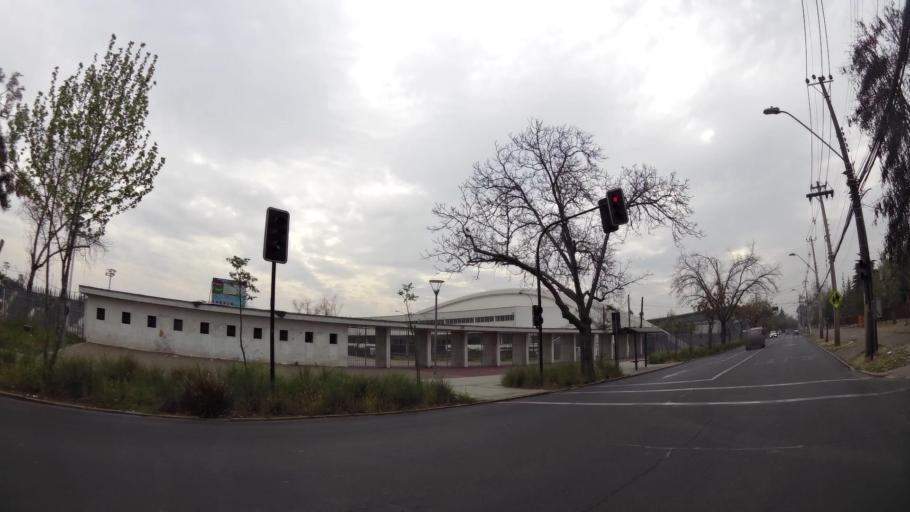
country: CL
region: Santiago Metropolitan
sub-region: Provincia de Santiago
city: Villa Presidente Frei, Nunoa, Santiago, Chile
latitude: -33.4687
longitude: -70.6066
